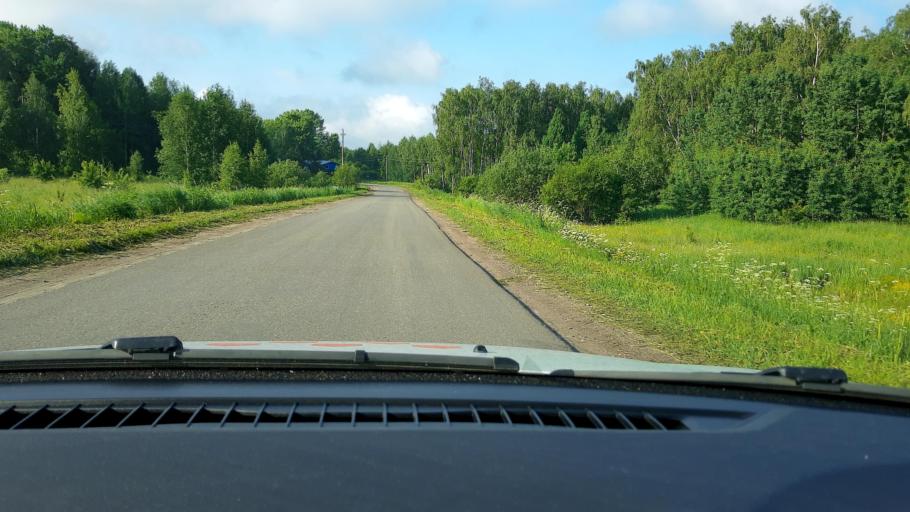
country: RU
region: Nizjnij Novgorod
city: Burevestnik
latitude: 56.1218
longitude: 43.8898
